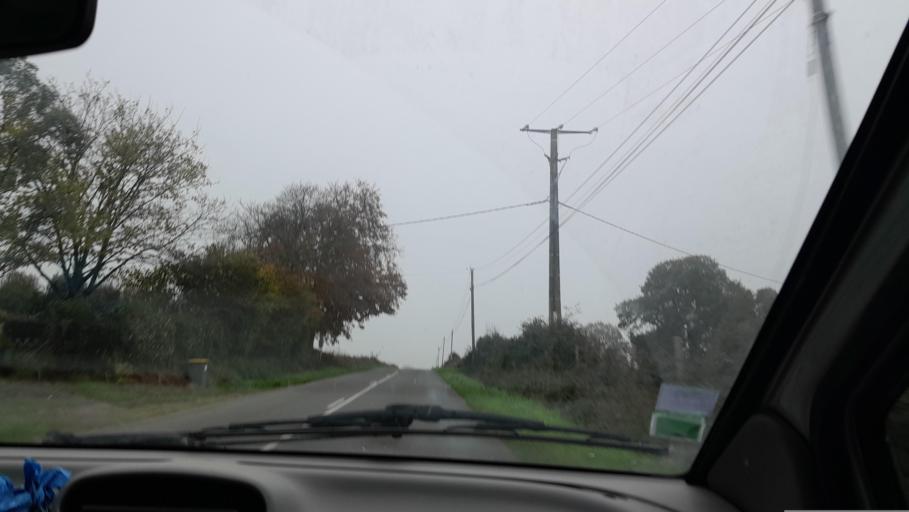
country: FR
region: Pays de la Loire
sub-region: Departement de la Mayenne
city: Ahuille
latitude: 48.0300
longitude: -0.9102
